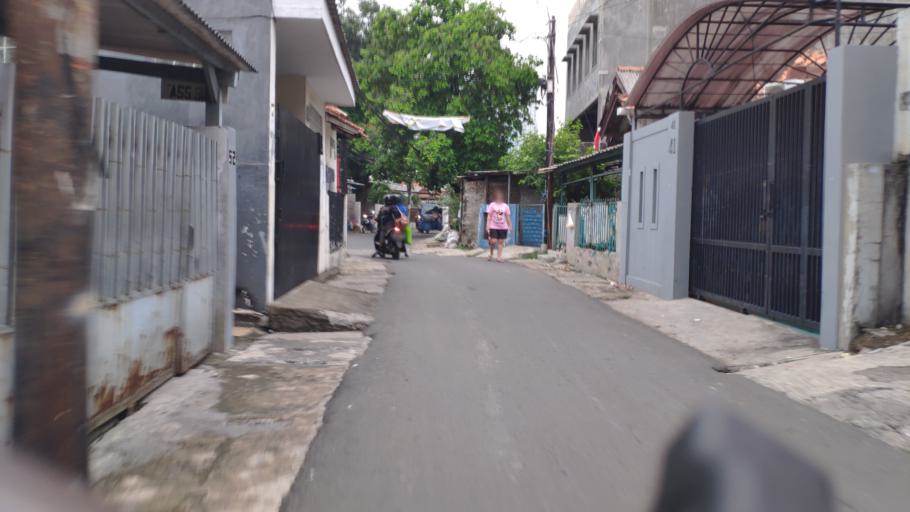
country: ID
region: Jakarta Raya
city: Jakarta
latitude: -6.2107
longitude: 106.8382
